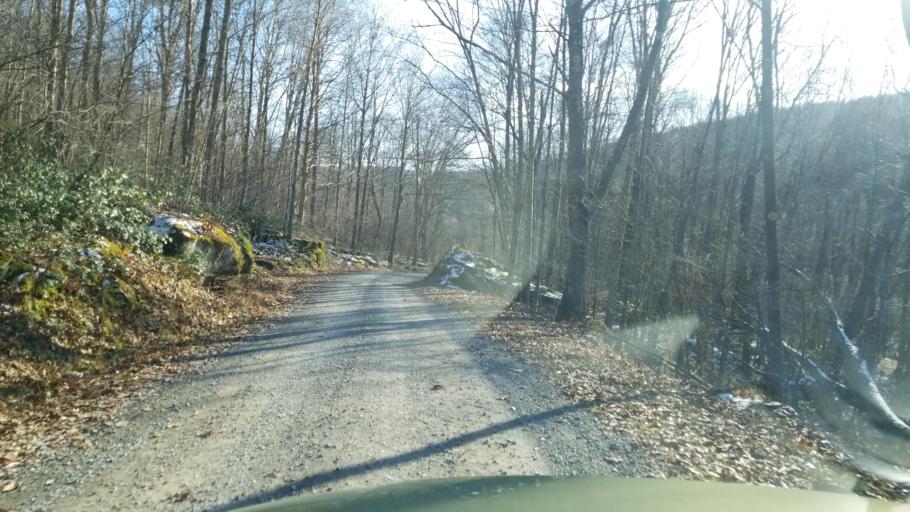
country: US
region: Pennsylvania
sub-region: Jefferson County
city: Brockway
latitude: 41.2835
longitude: -78.8264
